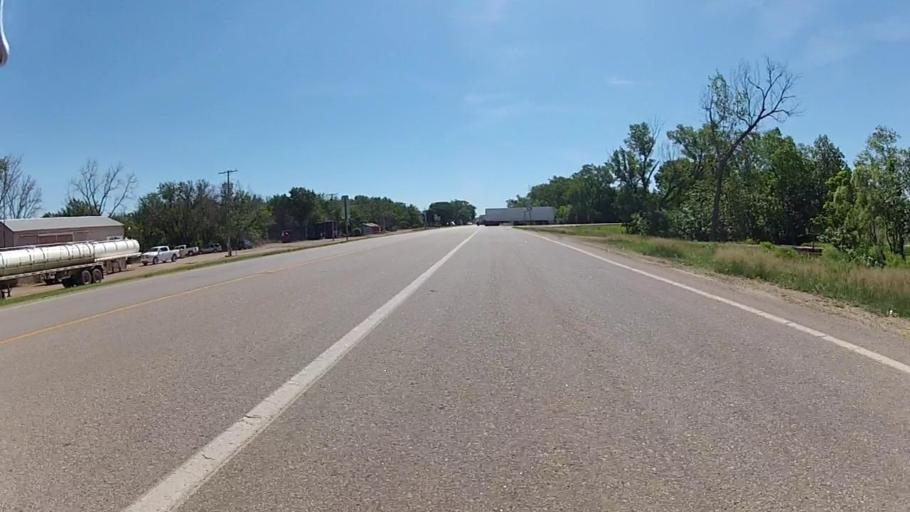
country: US
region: Kansas
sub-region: Barber County
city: Medicine Lodge
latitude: 37.2751
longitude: -98.5993
